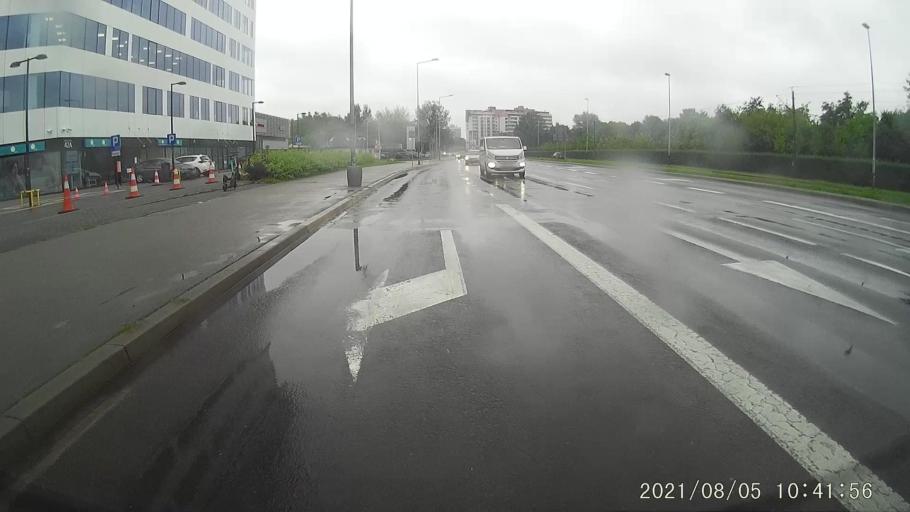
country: PL
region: Lesser Poland Voivodeship
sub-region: Krakow
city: Krakow
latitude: 50.0353
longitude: 19.9254
